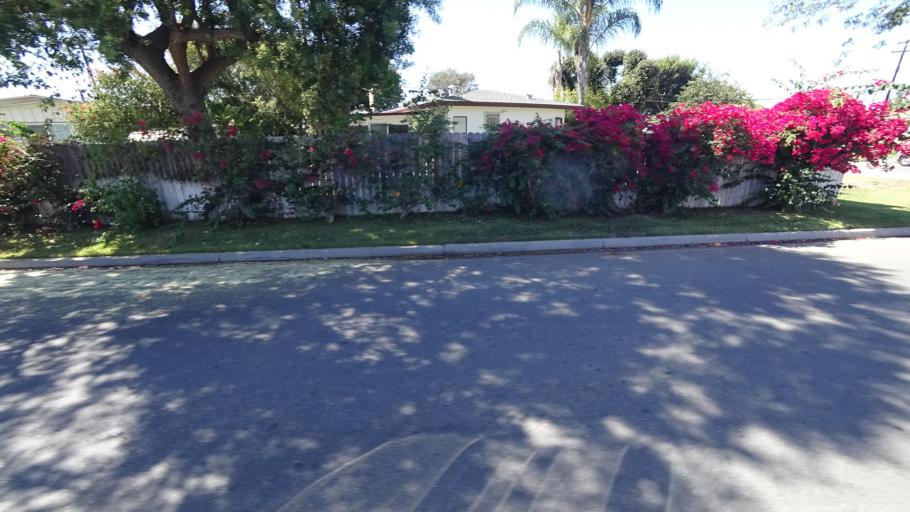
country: US
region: California
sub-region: Orange County
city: Garden Grove
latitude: 33.7917
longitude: -117.9621
